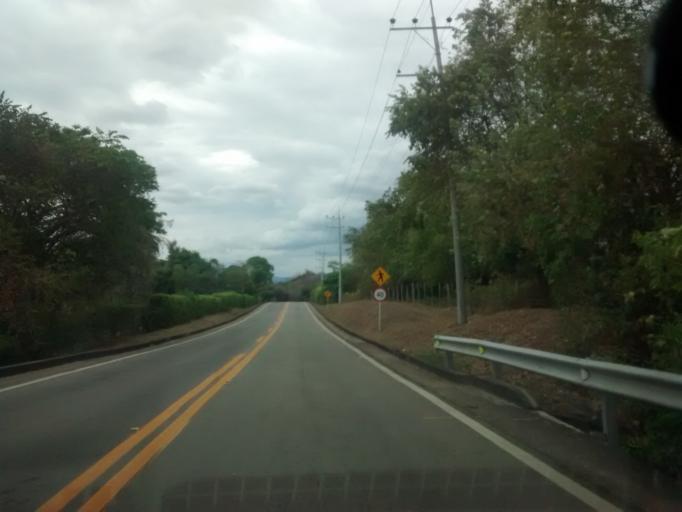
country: CO
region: Cundinamarca
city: Tocaima
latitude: 4.4368
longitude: -74.6799
